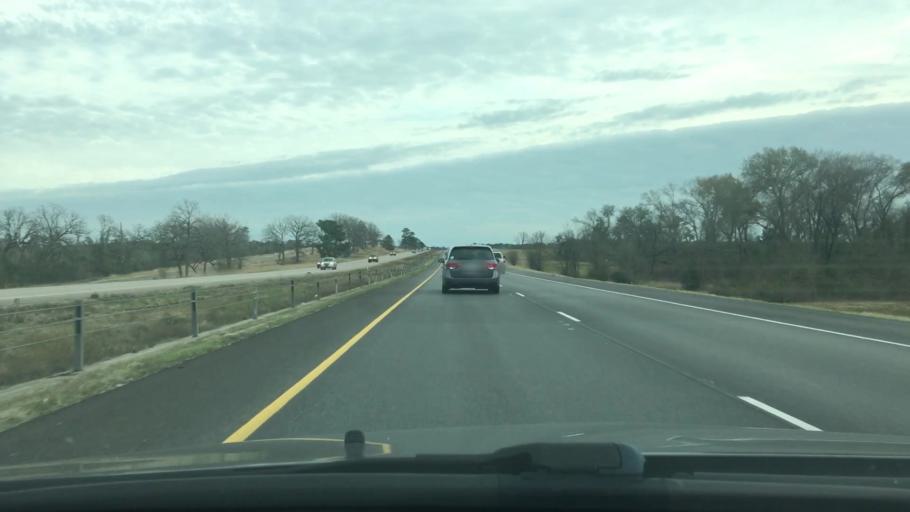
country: US
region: Texas
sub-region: Madison County
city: Madisonville
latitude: 30.8485
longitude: -95.7346
